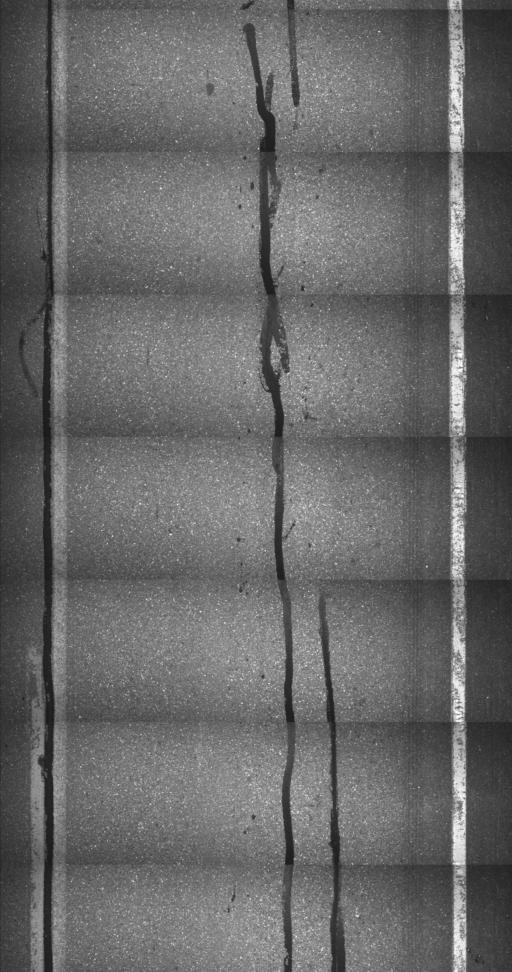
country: US
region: Vermont
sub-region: Orleans County
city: Newport
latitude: 44.9839
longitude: -72.4105
